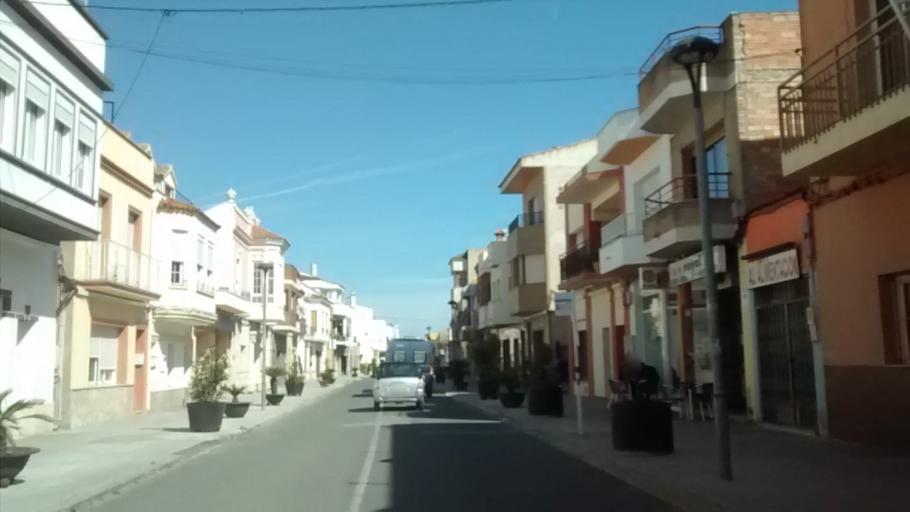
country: ES
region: Catalonia
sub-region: Provincia de Tarragona
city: Deltebre
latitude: 40.7168
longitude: 0.7371
